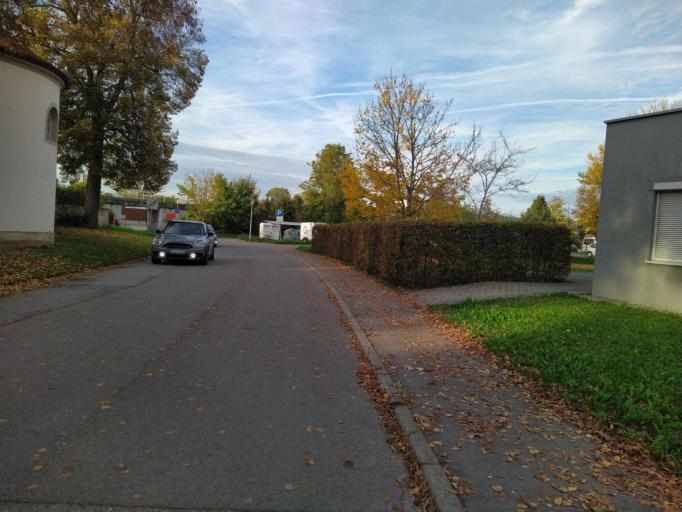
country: DE
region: Baden-Wuerttemberg
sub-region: Tuebingen Region
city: Rottenburg
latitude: 48.4782
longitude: 8.9726
